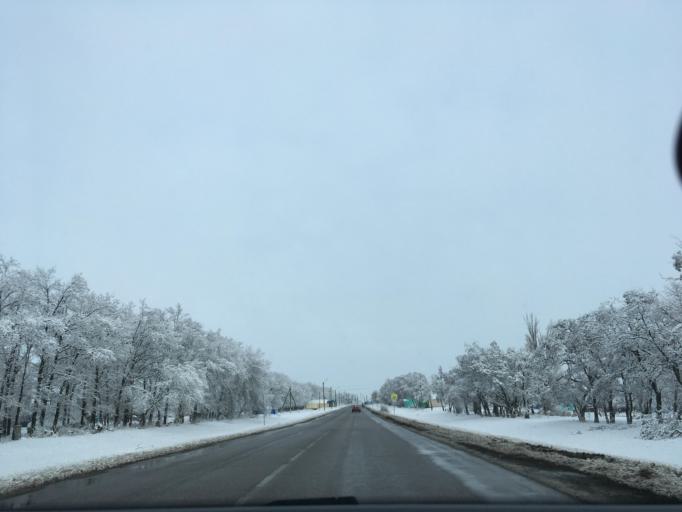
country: RU
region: Voronezj
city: Ol'khovatka
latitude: 50.0362
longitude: 39.0750
